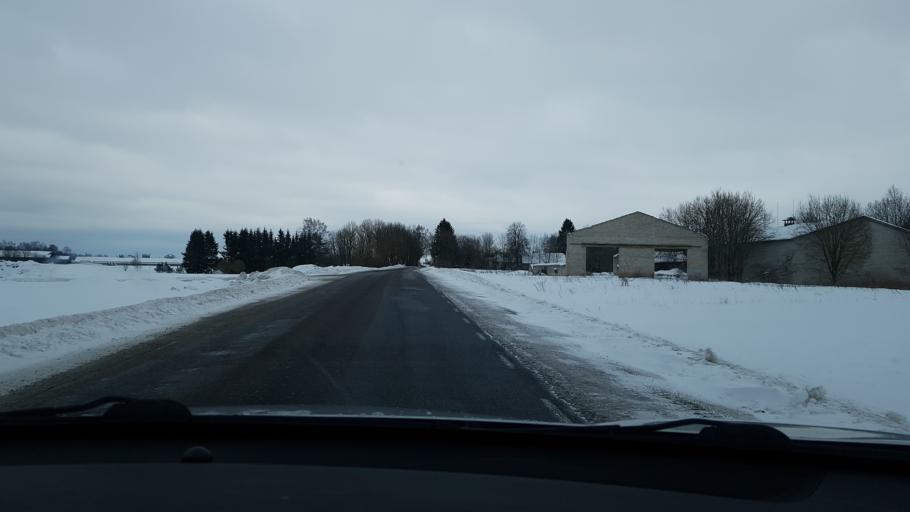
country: EE
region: Jaervamaa
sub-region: Koeru vald
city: Koeru
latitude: 58.9755
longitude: 26.0027
